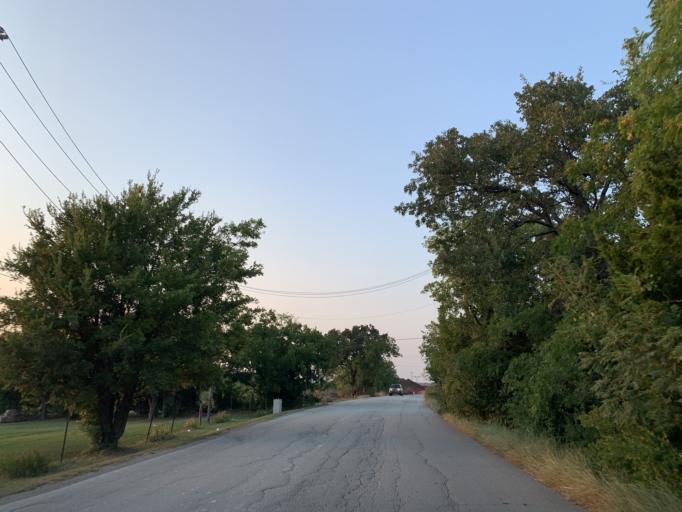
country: US
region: Texas
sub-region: Tarrant County
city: Keller
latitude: 32.9547
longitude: -97.2552
